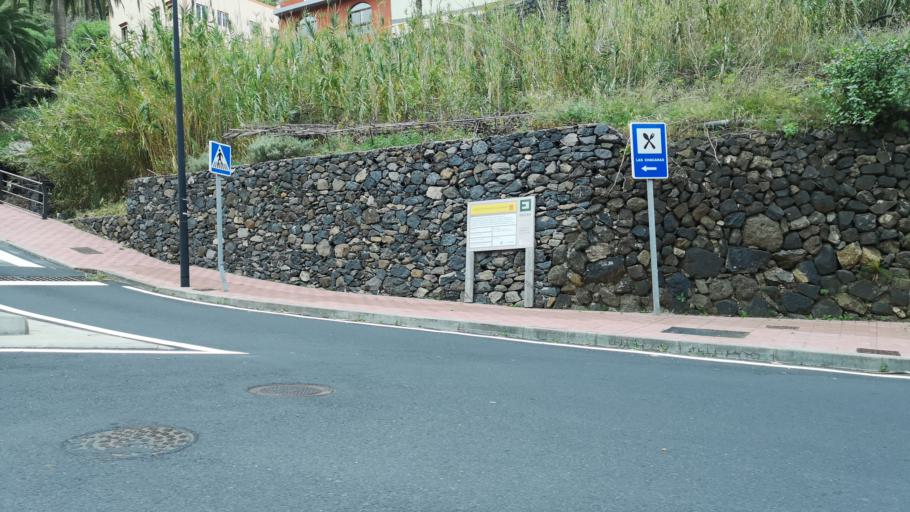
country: ES
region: Canary Islands
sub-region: Provincia de Santa Cruz de Tenerife
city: Hermigua
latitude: 28.1486
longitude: -17.1988
